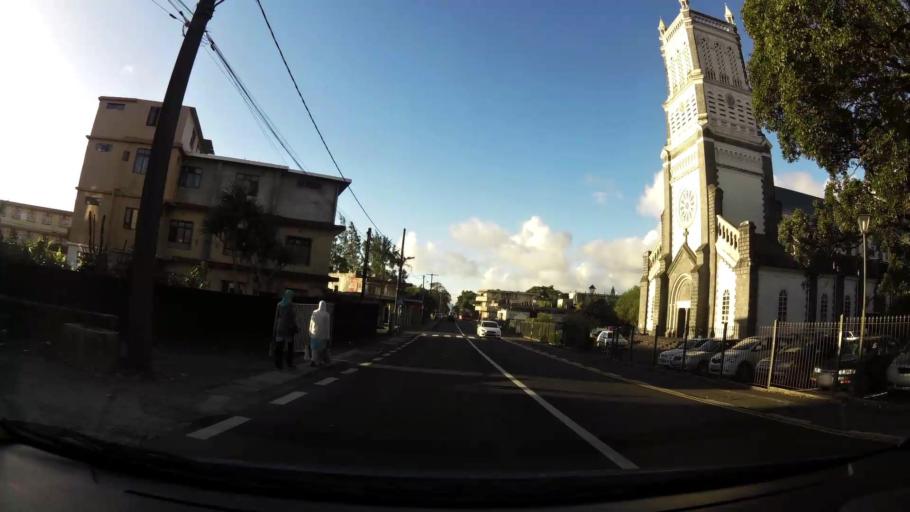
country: MU
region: Plaines Wilhems
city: Curepipe
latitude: -20.3117
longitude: 57.5241
